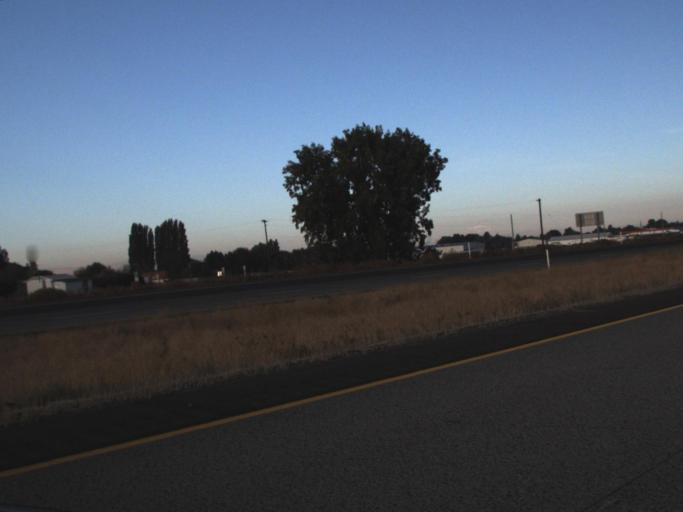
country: US
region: Washington
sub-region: Yakima County
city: Grandview
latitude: 46.2526
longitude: -119.8718
